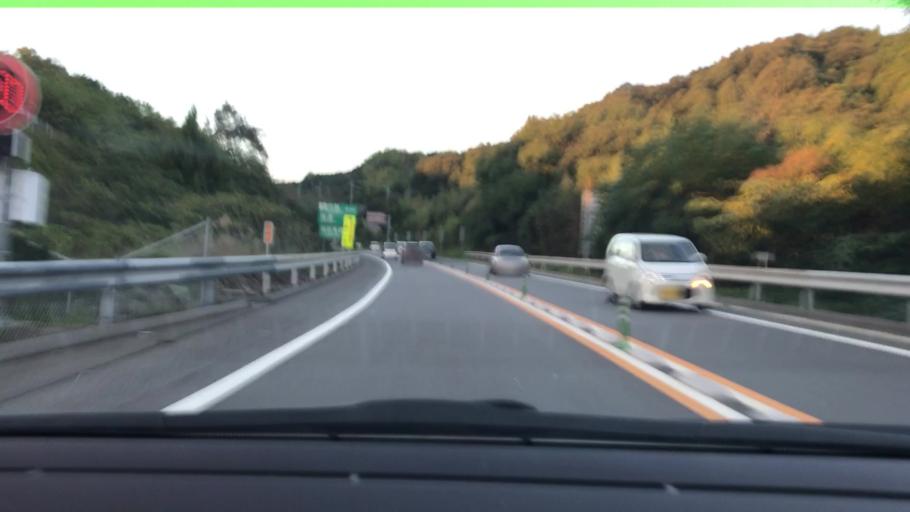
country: JP
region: Hiroshima
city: Innoshima
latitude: 34.3395
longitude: 133.1612
